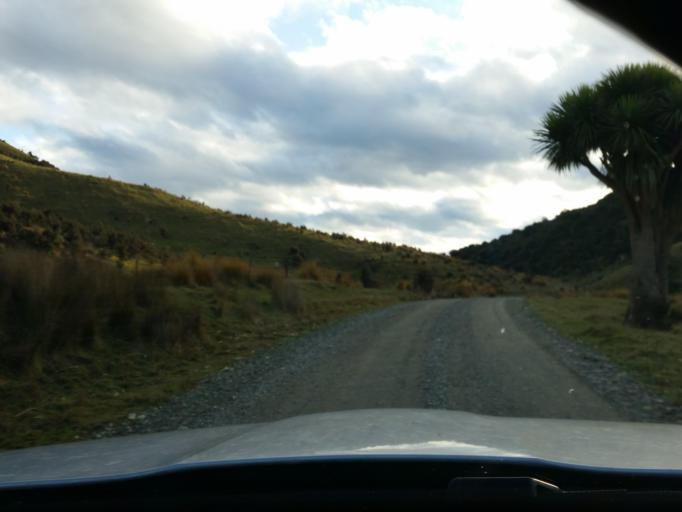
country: NZ
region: Southland
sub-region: Southland District
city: Te Anau
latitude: -45.8437
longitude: 167.6754
